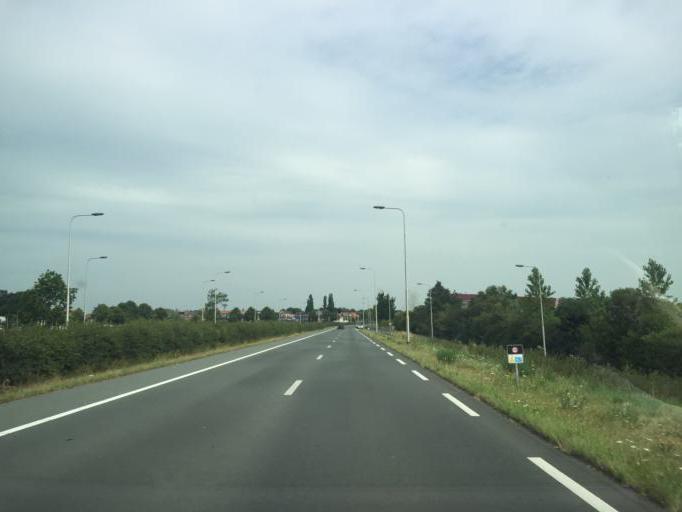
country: NL
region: North Holland
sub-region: Gemeente Bloemendaal
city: Bloemendaal
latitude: 52.4265
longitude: 4.6456
